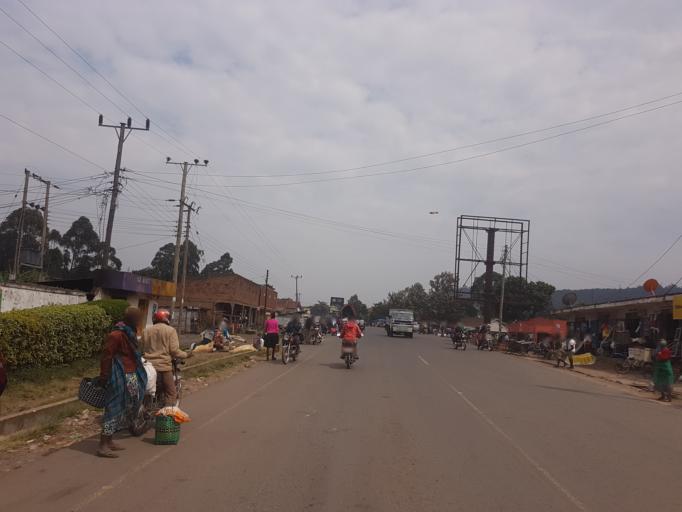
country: UG
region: Western Region
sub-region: Kisoro District
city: Kisoro
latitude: -1.2828
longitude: 29.7006
